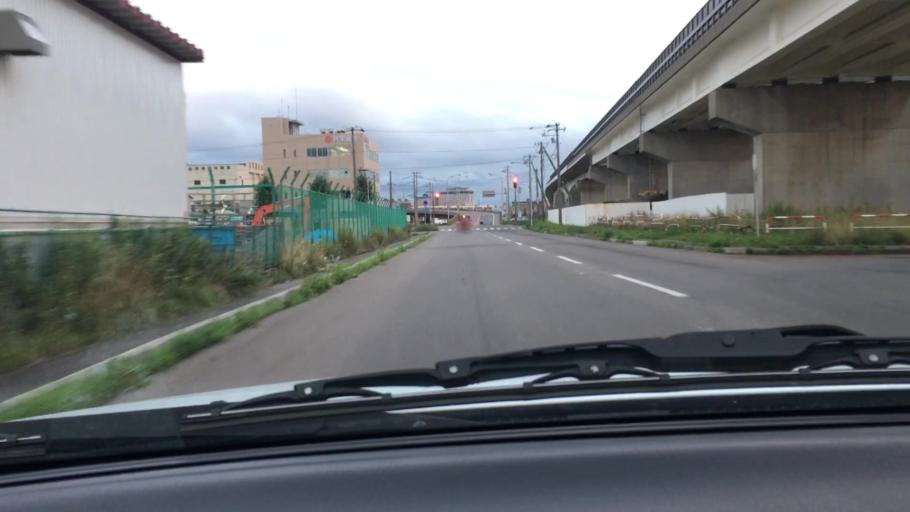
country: JP
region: Hokkaido
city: Hakodate
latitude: 41.7841
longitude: 140.7271
